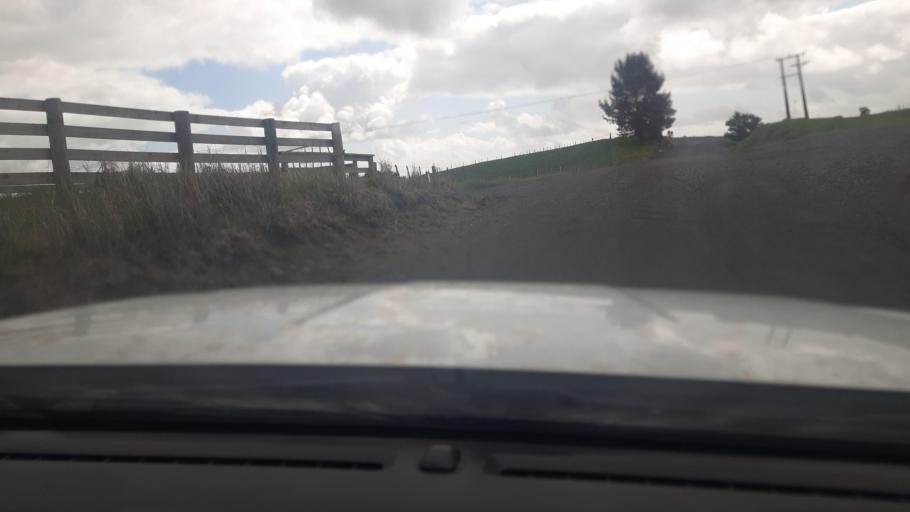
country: NZ
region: Northland
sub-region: Far North District
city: Kaitaia
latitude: -35.0634
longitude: 173.3238
